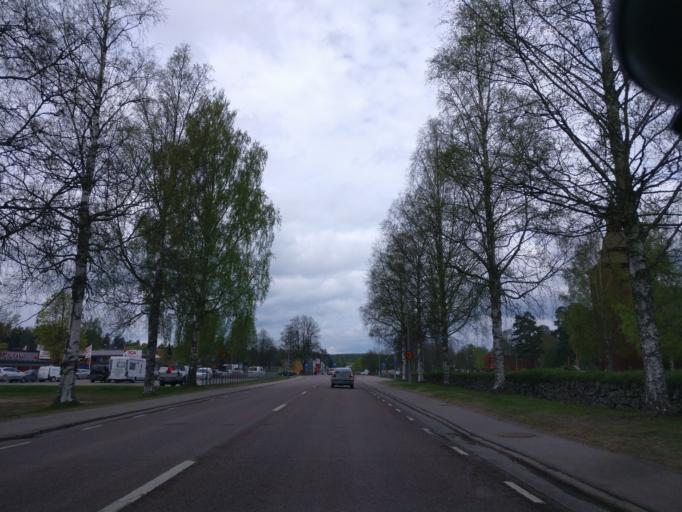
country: SE
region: Vaermland
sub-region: Hagfors Kommun
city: Ekshaerad
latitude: 60.1717
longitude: 13.4968
